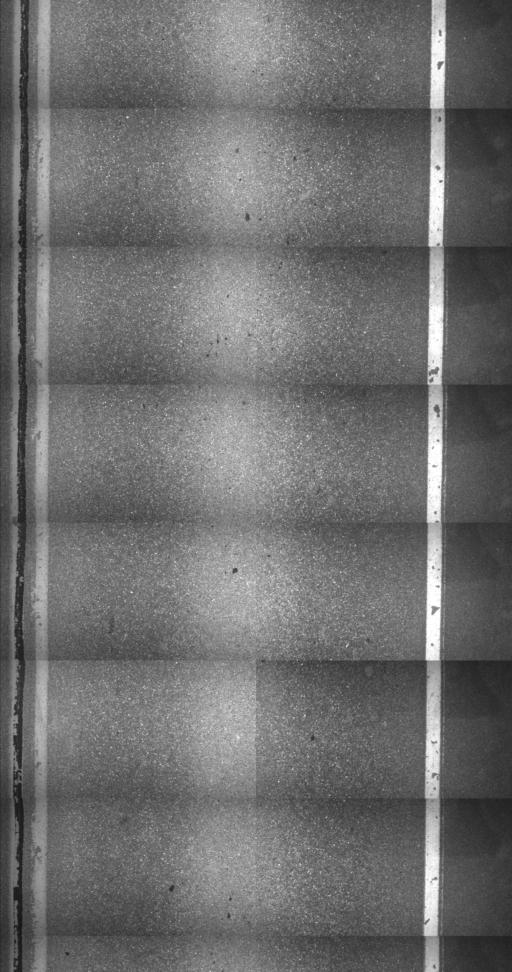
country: US
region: Vermont
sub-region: Chittenden County
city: Milton
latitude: 44.6310
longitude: -73.0189
